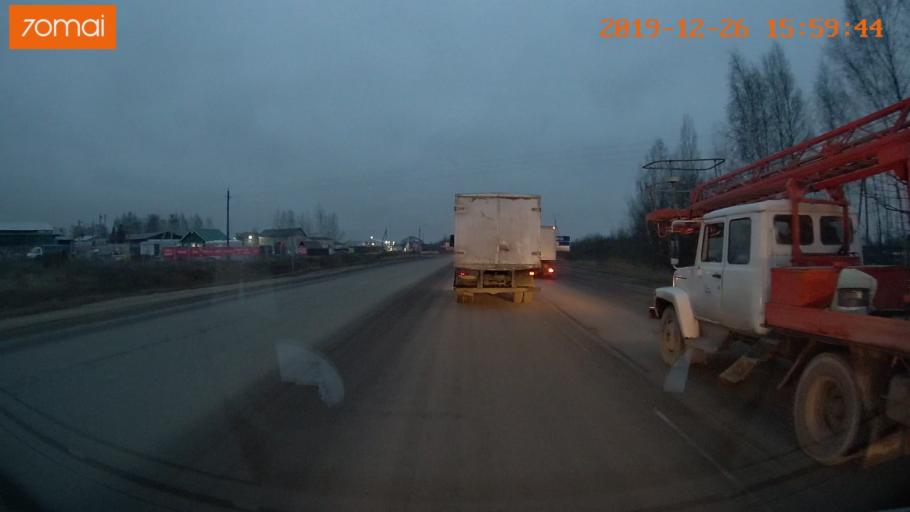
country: RU
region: Jaroslavl
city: Rybinsk
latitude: 58.0298
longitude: 38.8046
